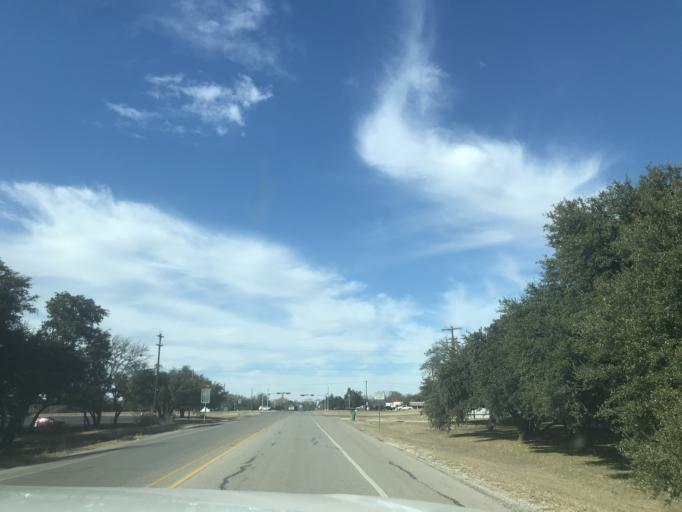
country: US
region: Texas
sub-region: Erath County
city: Stephenville
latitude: 32.2101
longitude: -98.1950
